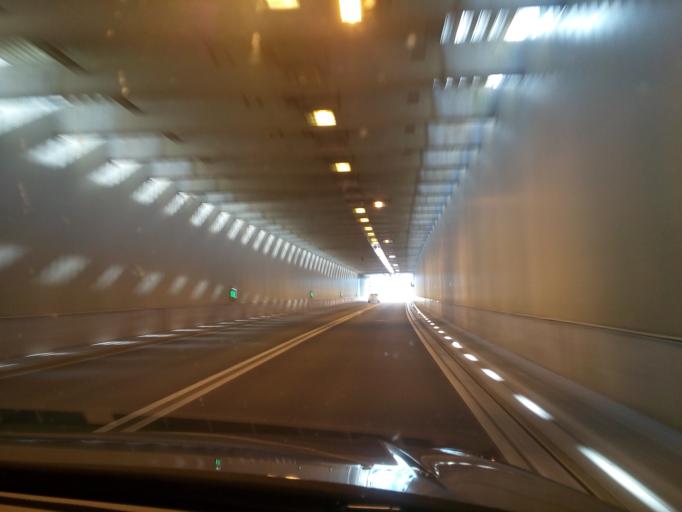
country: DE
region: Baden-Wuerttemberg
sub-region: Freiburg Region
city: Oberkirch
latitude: 48.5216
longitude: 8.0822
